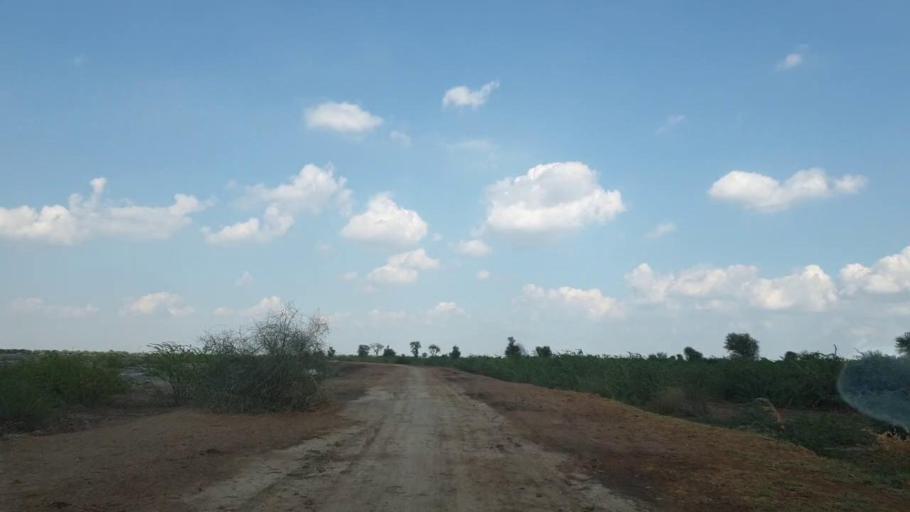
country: PK
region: Sindh
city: Pithoro
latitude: 25.6037
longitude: 69.3691
